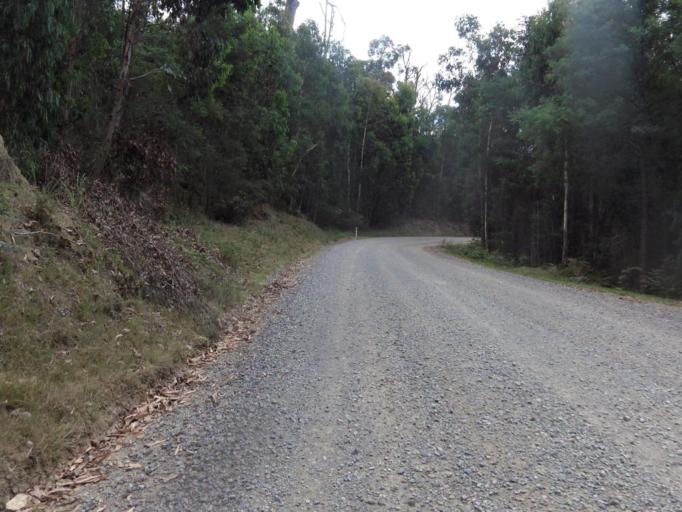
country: AU
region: Victoria
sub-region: Yarra Ranges
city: Healesville
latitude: -37.4198
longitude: 145.5640
